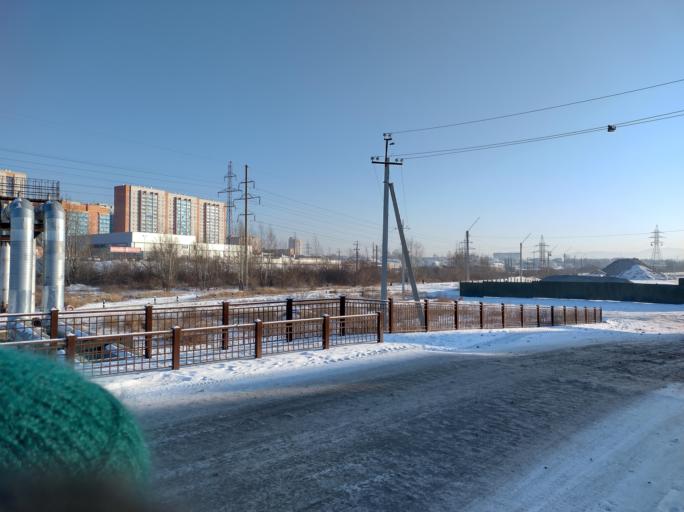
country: RU
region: Transbaikal Territory
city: Chita
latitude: 52.0784
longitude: 113.4716
